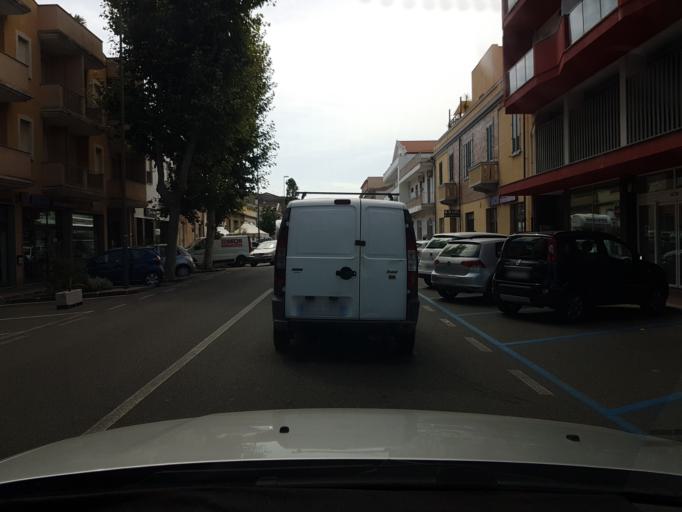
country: IT
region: Sardinia
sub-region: Provincia di Oristano
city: Oristano
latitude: 39.9090
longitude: 8.5893
